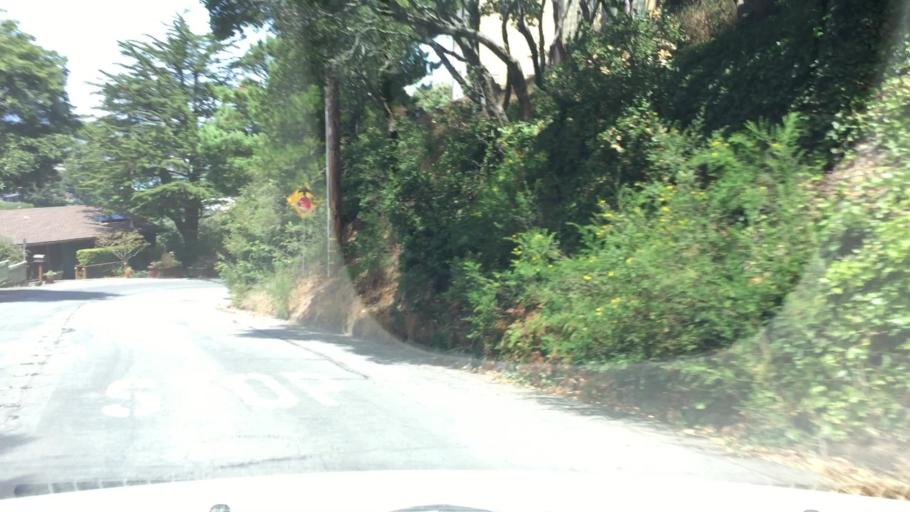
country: US
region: California
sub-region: Marin County
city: Sausalito
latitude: 37.8527
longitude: -122.4884
